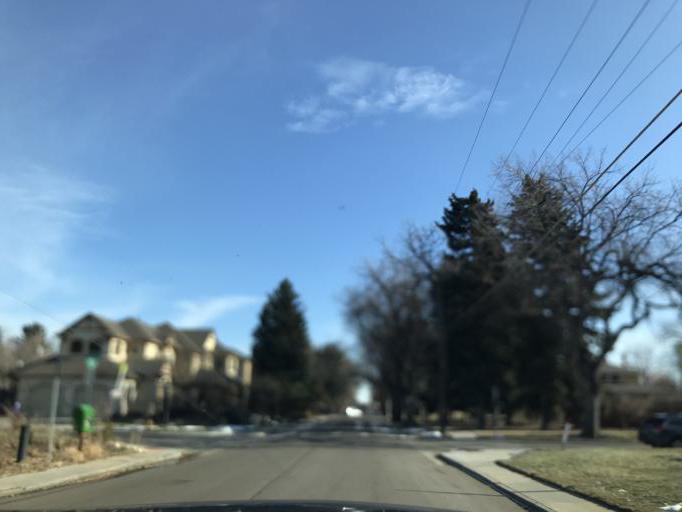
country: US
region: Colorado
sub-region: Arapahoe County
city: Glendale
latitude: 39.7356
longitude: -104.9098
